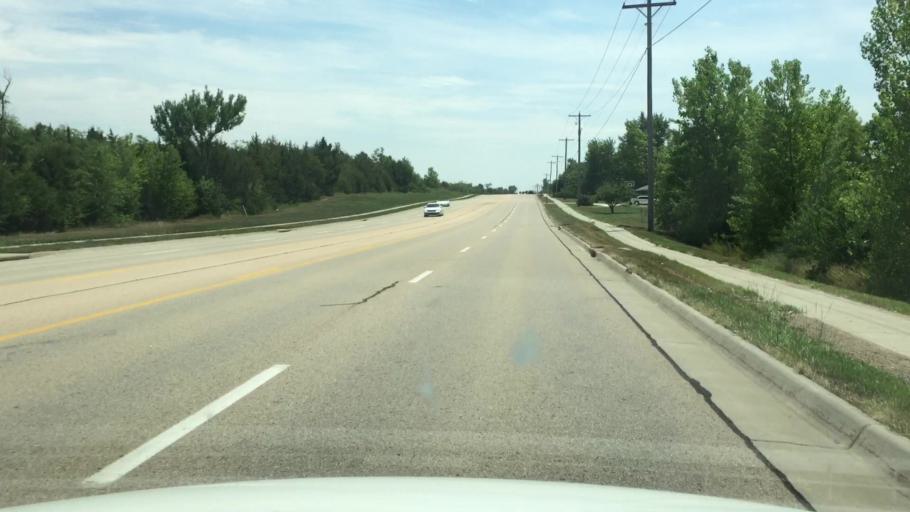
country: US
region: Kansas
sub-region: Shawnee County
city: Topeka
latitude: 38.9955
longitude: -95.6145
